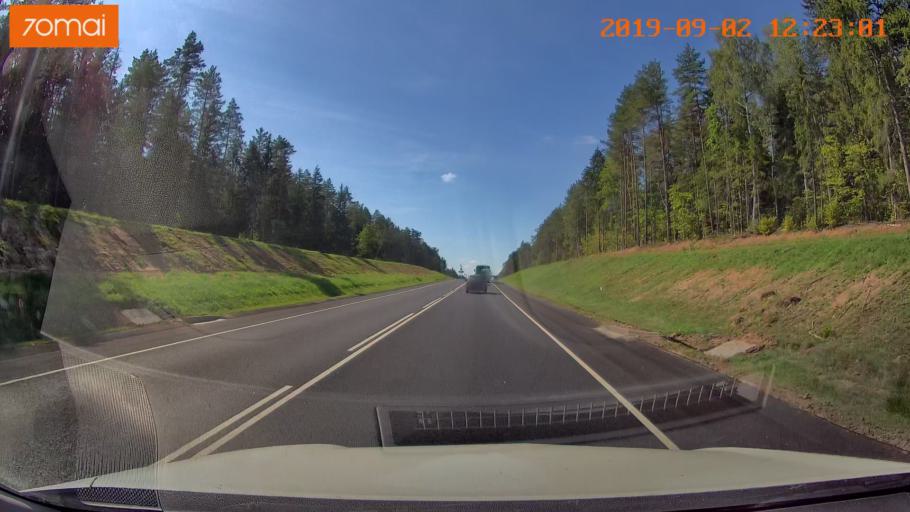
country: RU
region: Smolensk
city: Shumyachi
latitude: 53.8771
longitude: 32.6254
